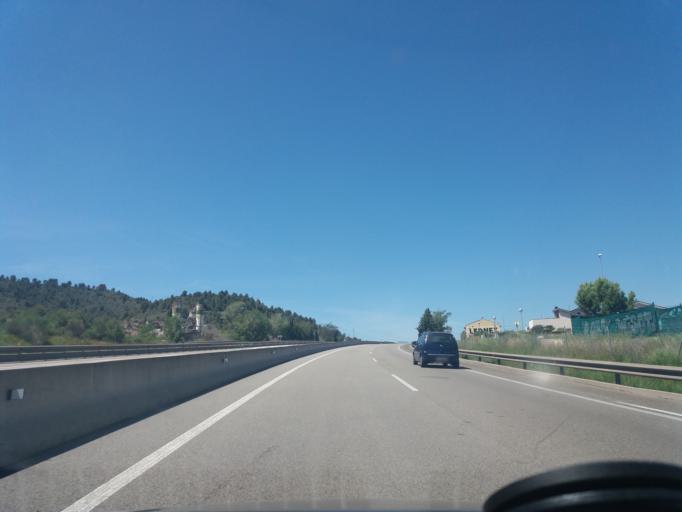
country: ES
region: Catalonia
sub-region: Provincia de Barcelona
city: Sallent
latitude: 41.8191
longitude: 1.8921
